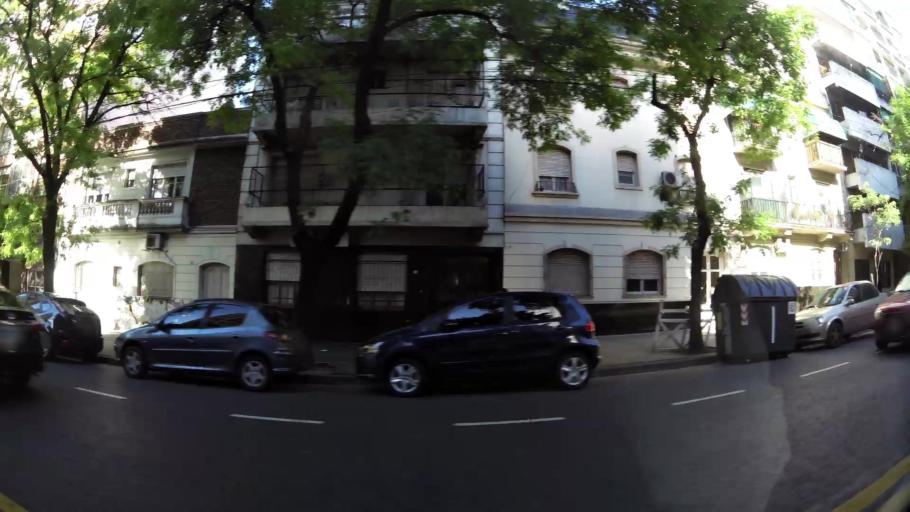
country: AR
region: Buenos Aires F.D.
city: Colegiales
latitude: -34.6124
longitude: -58.4385
